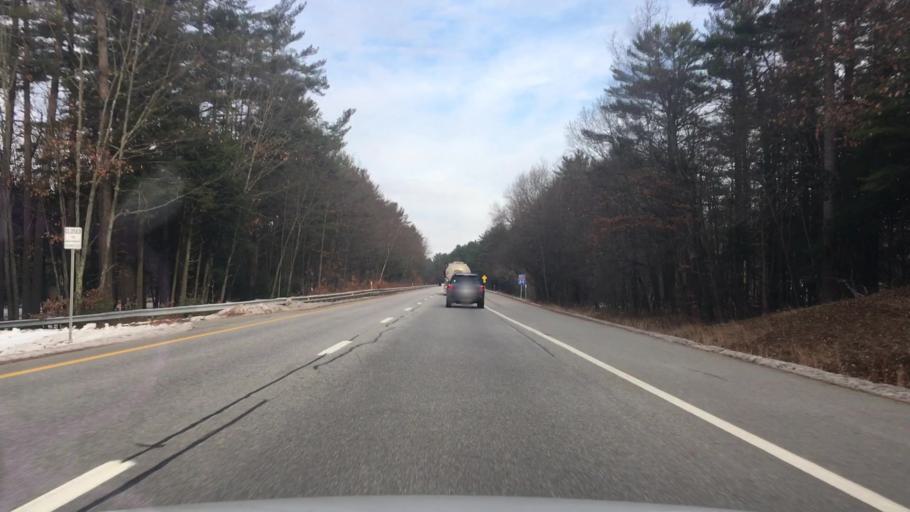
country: US
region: New Hampshire
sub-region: Merrimack County
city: Contoocook
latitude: 43.2079
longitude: -71.7114
